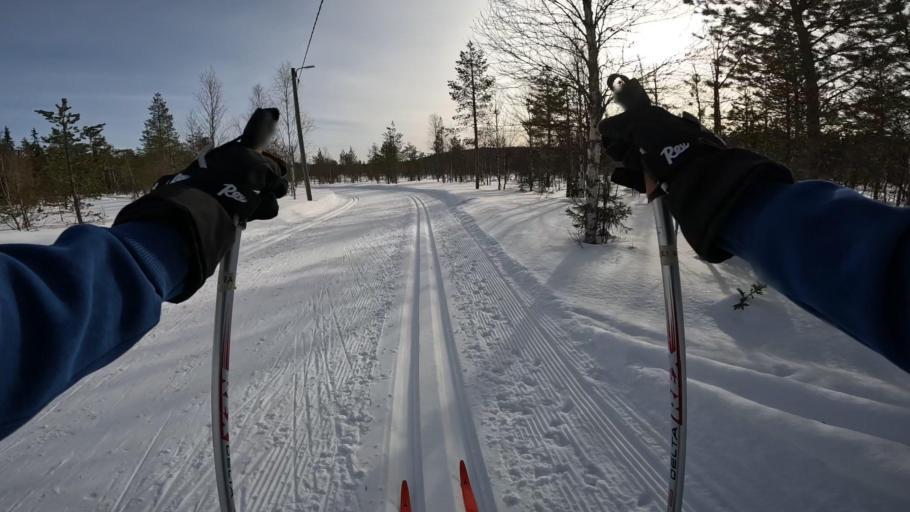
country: FI
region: Lapland
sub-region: Itae-Lappi
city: Salla
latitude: 66.7521
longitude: 28.7856
